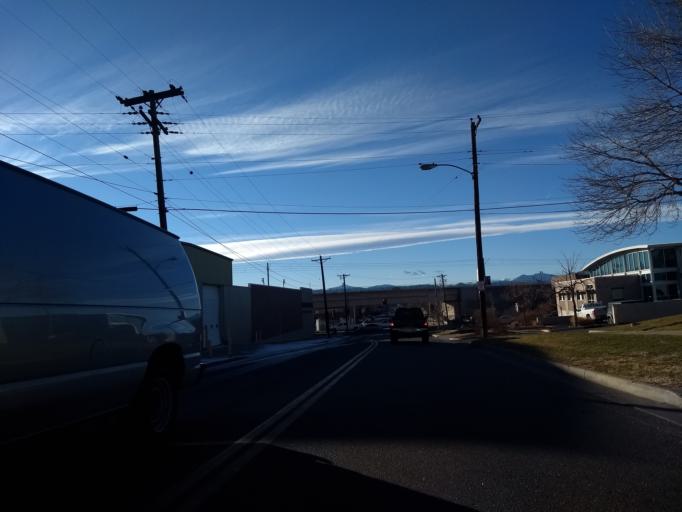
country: US
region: Colorado
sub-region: Denver County
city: Denver
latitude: 39.7210
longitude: -104.9990
